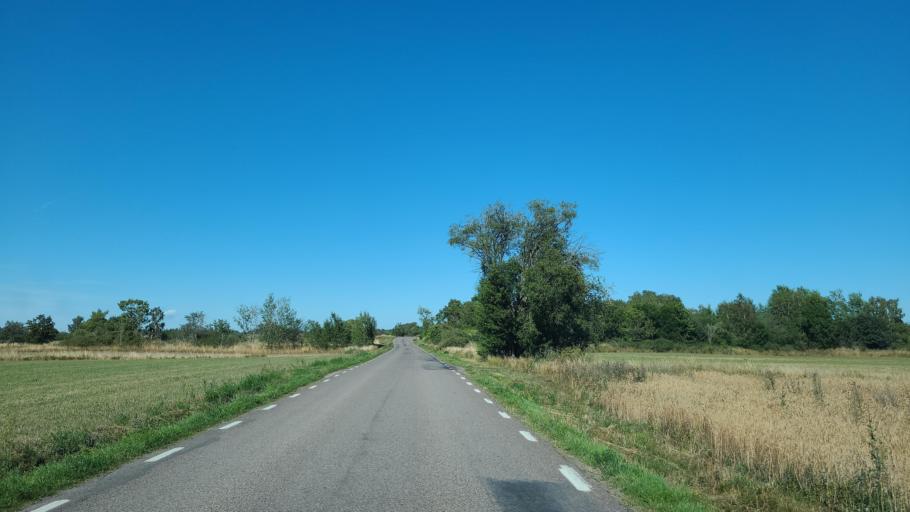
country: SE
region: Kalmar
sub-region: Borgholms Kommun
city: Borgholm
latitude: 56.8547
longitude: 16.8098
